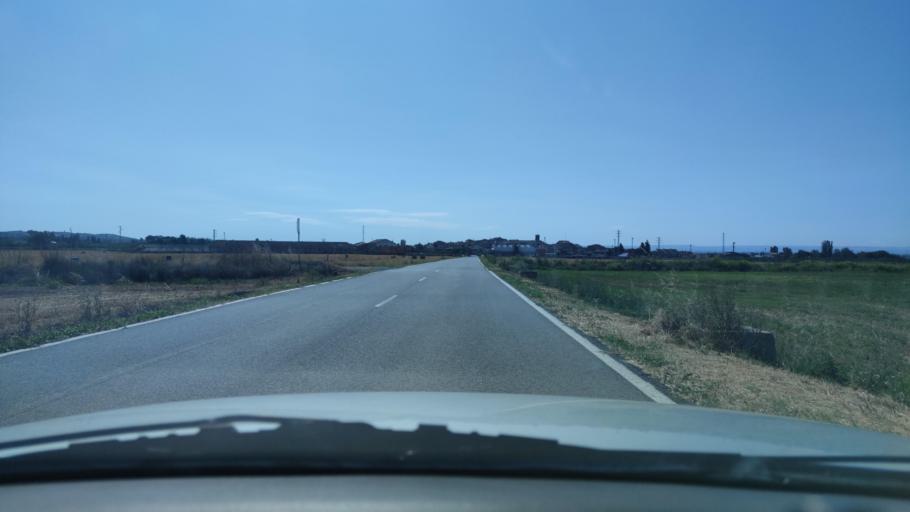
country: ES
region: Catalonia
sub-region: Provincia de Lleida
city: Penelles
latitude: 41.7513
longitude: 0.9784
